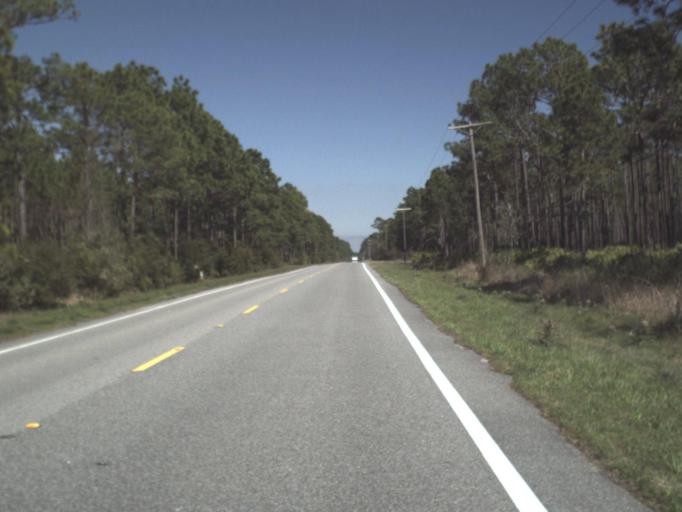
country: US
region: Florida
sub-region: Franklin County
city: Carrabelle
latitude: 29.9223
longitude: -84.4905
